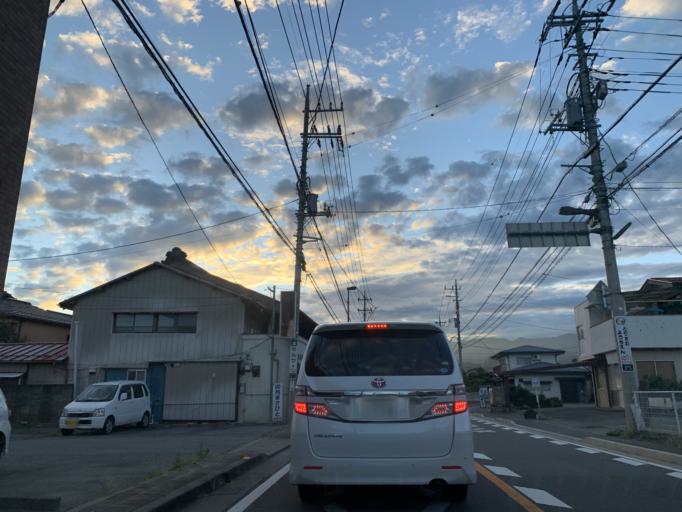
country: JP
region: Yamanashi
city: Otsuki
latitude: 35.6087
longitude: 139.0034
